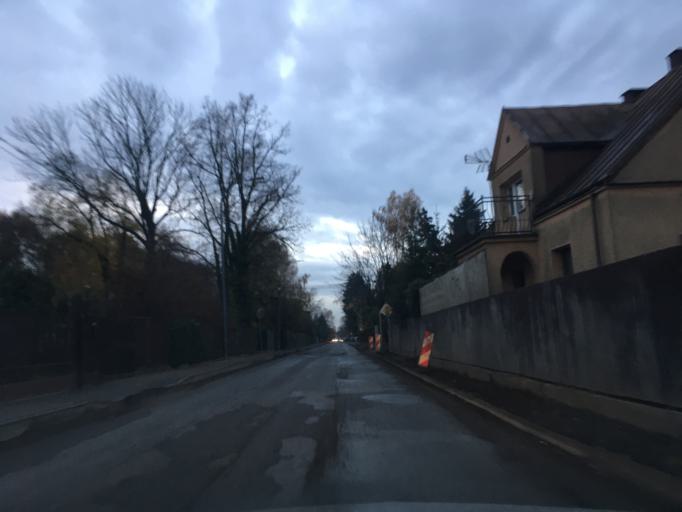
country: PL
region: Masovian Voivodeship
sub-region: Powiat piaseczynski
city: Piaseczno
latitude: 52.0549
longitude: 20.9844
